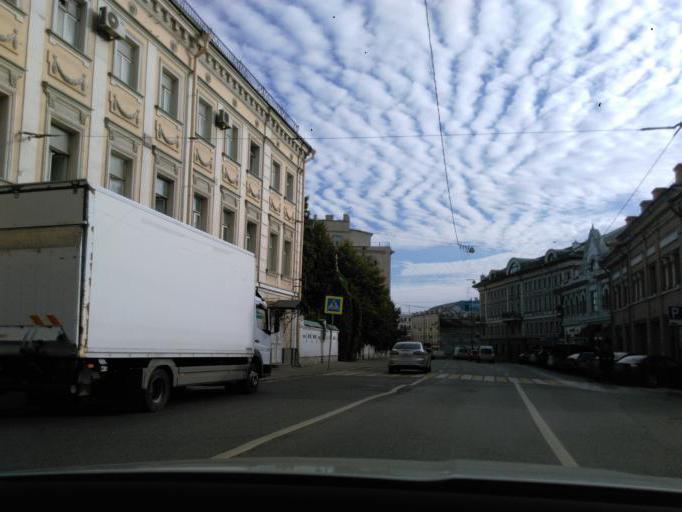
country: RU
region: Moscow
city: Moscow
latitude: 55.7649
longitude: 37.6301
